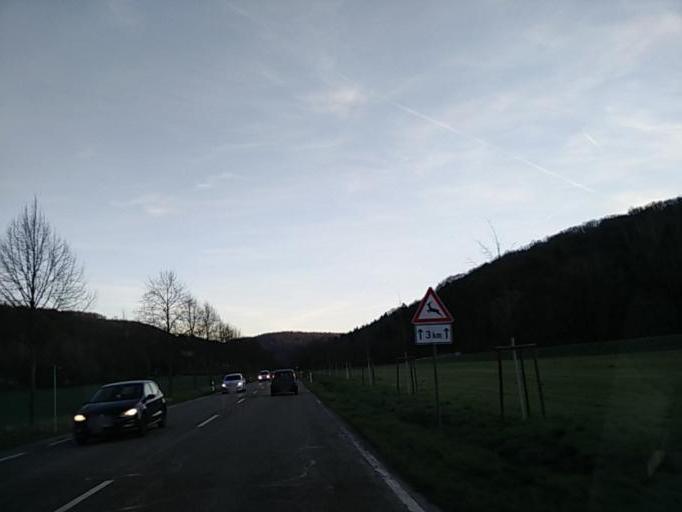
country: DE
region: Baden-Wuerttemberg
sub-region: Tuebingen Region
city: Tuebingen
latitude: 48.5363
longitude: 9.0770
